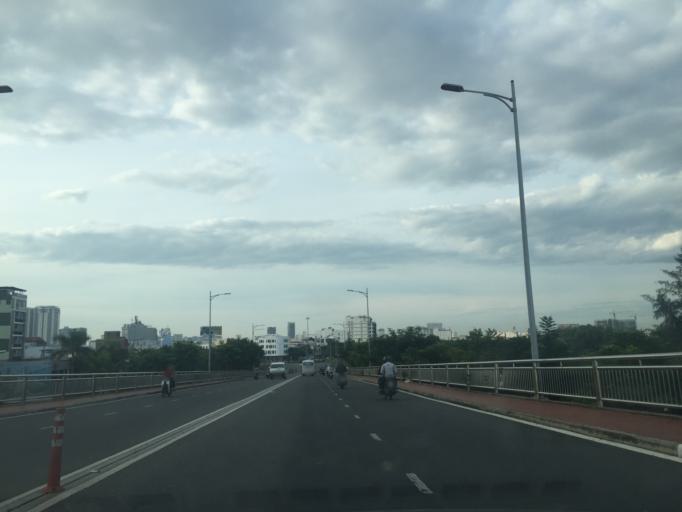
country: VN
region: Da Nang
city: Da Nang
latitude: 16.0909
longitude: 108.2149
